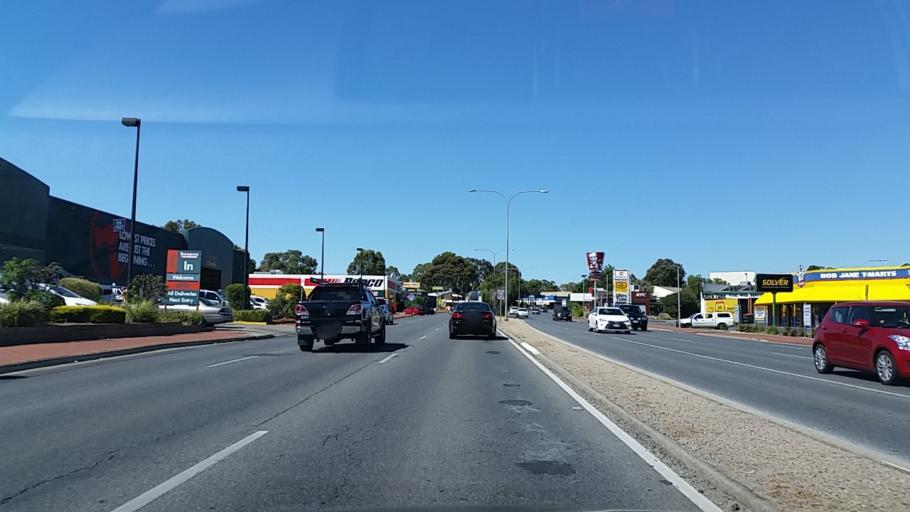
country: AU
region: South Australia
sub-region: Tea Tree Gully
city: Modbury
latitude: -34.8334
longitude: 138.6833
